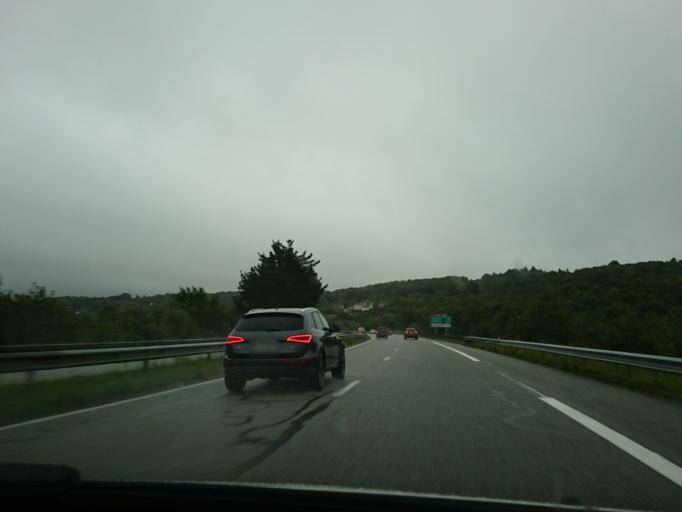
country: FR
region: Brittany
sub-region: Departement du Finistere
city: Ergue-Gaberic
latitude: 47.9920
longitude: -4.0445
